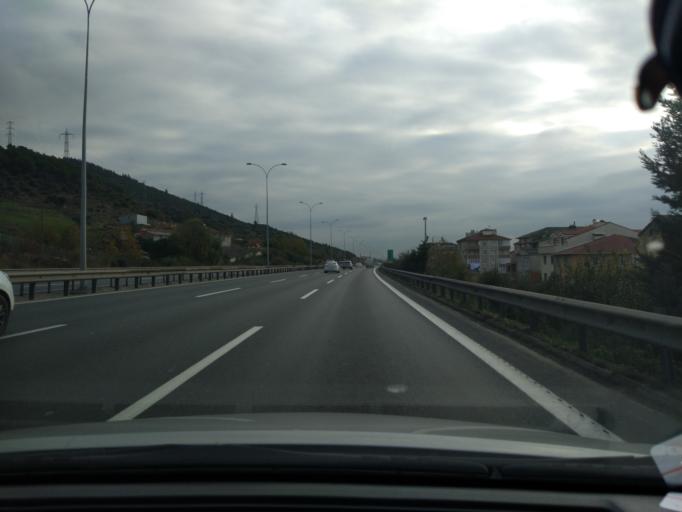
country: TR
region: Kocaeli
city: Korfez
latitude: 40.7781
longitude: 29.7452
